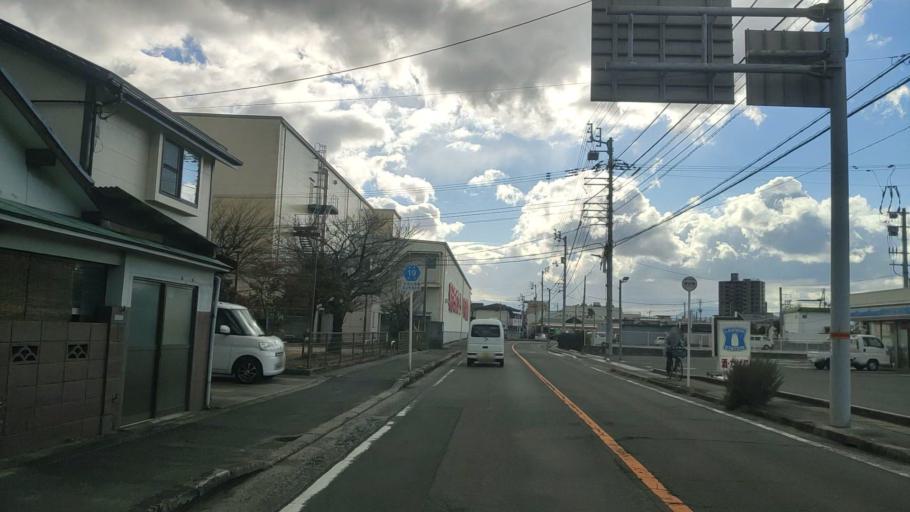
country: JP
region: Ehime
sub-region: Shikoku-chuo Shi
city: Matsuyama
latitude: 33.8668
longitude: 132.7188
